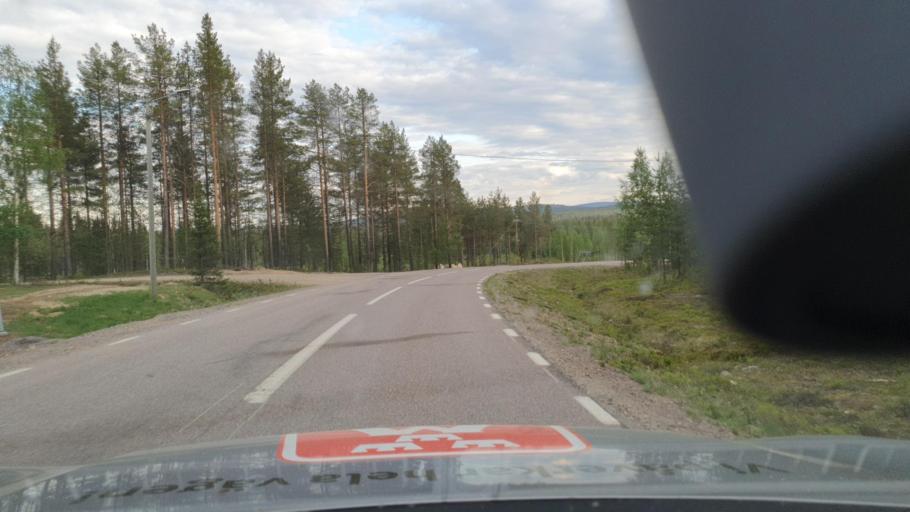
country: SE
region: Norrbotten
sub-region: Gallivare Kommun
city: Gaellivare
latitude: 66.9318
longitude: 21.2715
